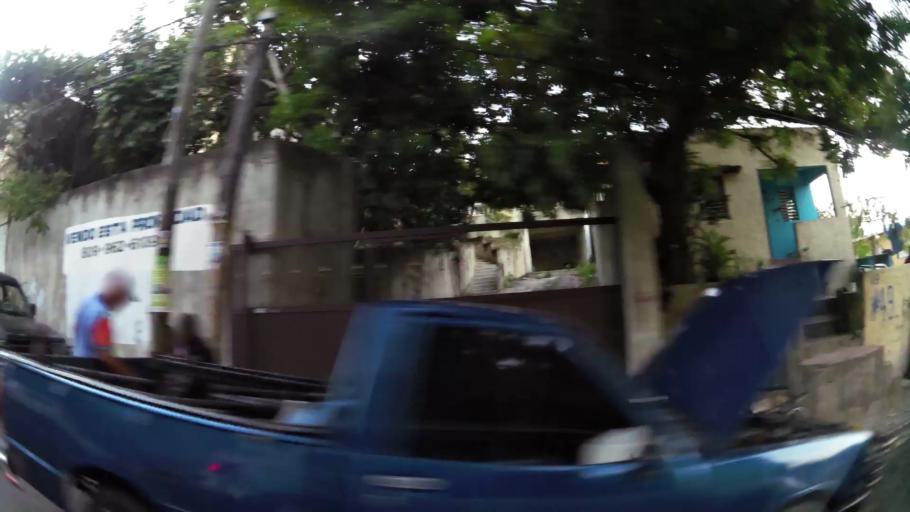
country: DO
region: Nacional
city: La Agustina
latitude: 18.5032
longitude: -69.9511
